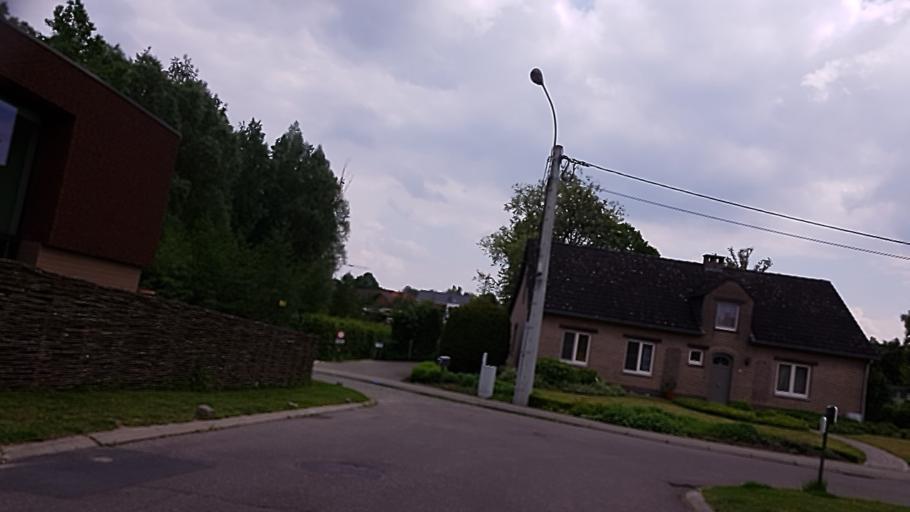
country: BE
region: Flanders
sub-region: Provincie Vlaams-Brabant
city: Bertem
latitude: 50.8488
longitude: 4.5870
